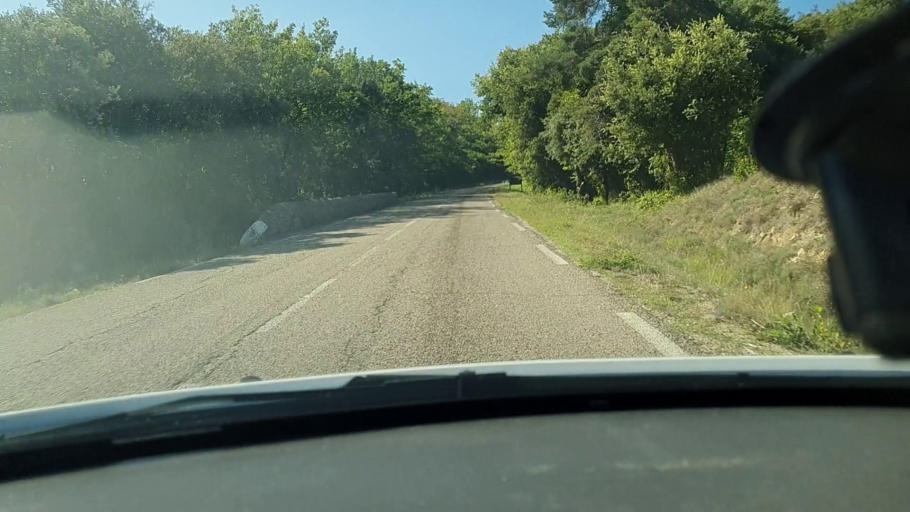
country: FR
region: Languedoc-Roussillon
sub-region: Departement du Gard
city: Saint-Paulet-de-Caisson
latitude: 44.2418
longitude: 4.5746
